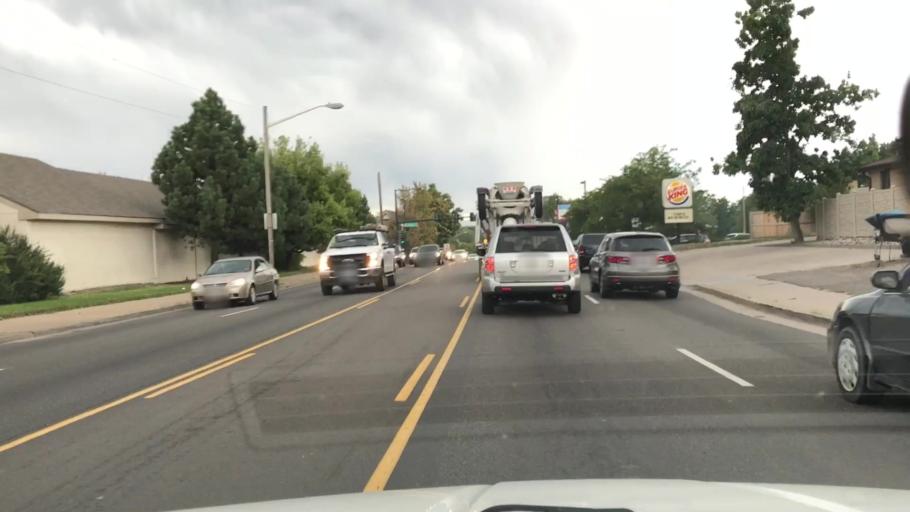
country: US
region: Colorado
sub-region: Jefferson County
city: Edgewater
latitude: 39.7561
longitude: -105.0533
